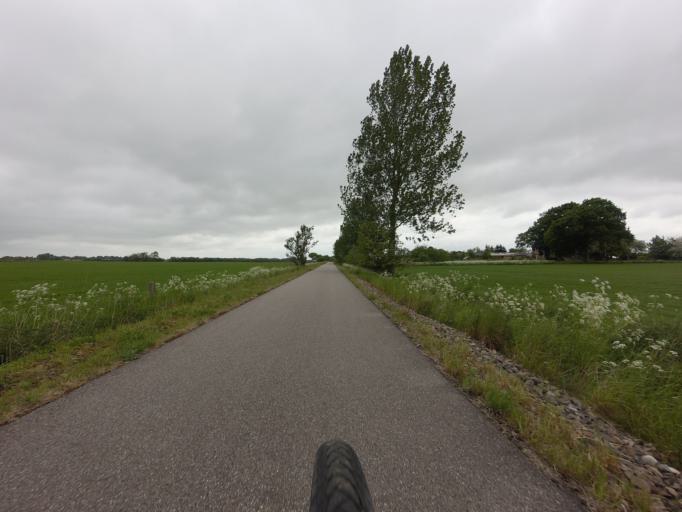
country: DK
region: Zealand
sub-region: Slagelse Kommune
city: Slagelse
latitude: 55.3009
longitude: 11.4152
